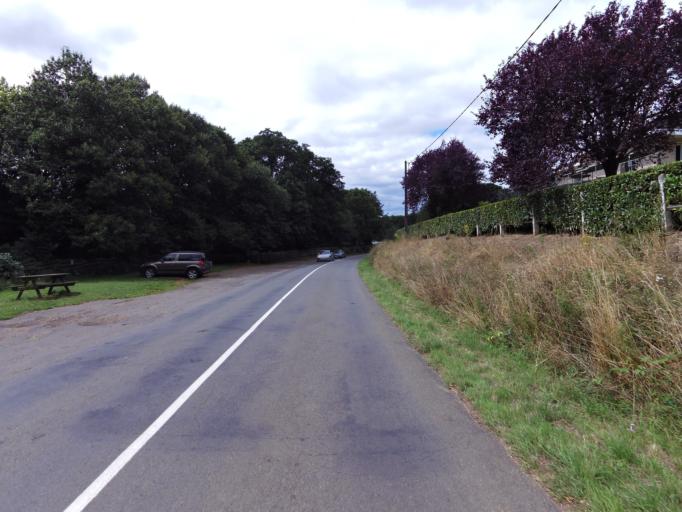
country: FR
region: Nord-Pas-de-Calais
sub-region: Departement du Nord
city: Saint-Jans-Cappel
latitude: 50.7804
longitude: 2.7254
